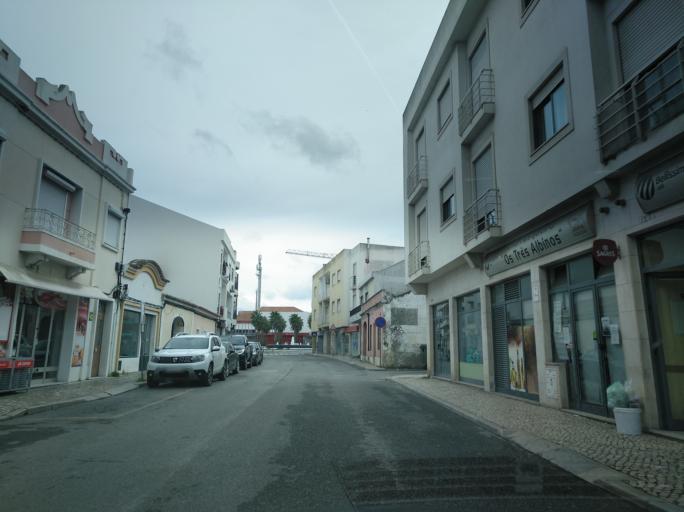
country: PT
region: Setubal
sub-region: Grandola
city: Grandola
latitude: 38.1781
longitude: -8.5671
